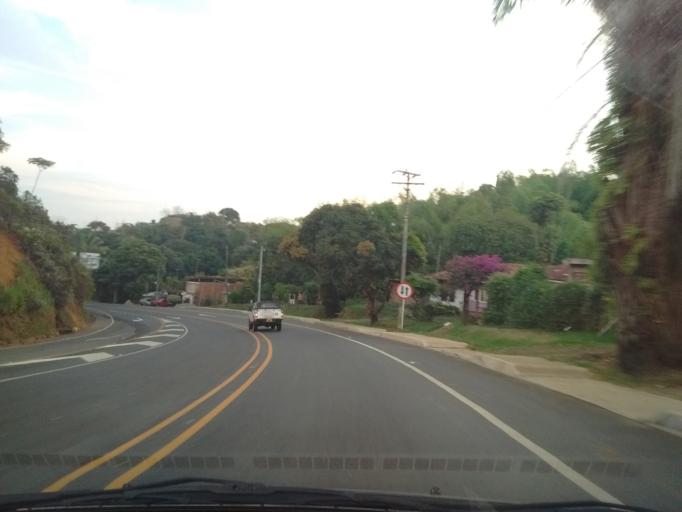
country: CO
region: Cauca
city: Santander de Quilichao
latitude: 2.9944
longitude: -76.4940
